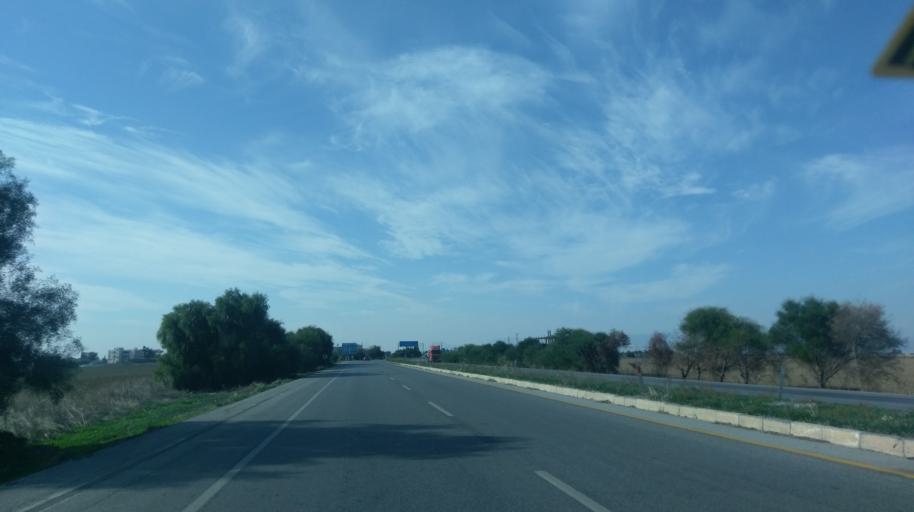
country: CY
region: Ammochostos
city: Lefkonoiko
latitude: 35.1730
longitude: 33.7703
